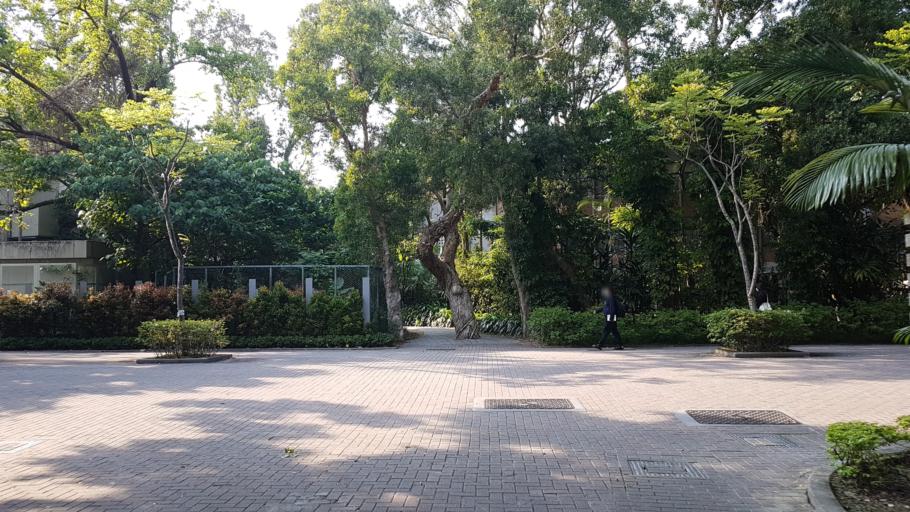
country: TW
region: Taipei
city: Taipei
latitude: 25.0149
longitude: 121.5368
